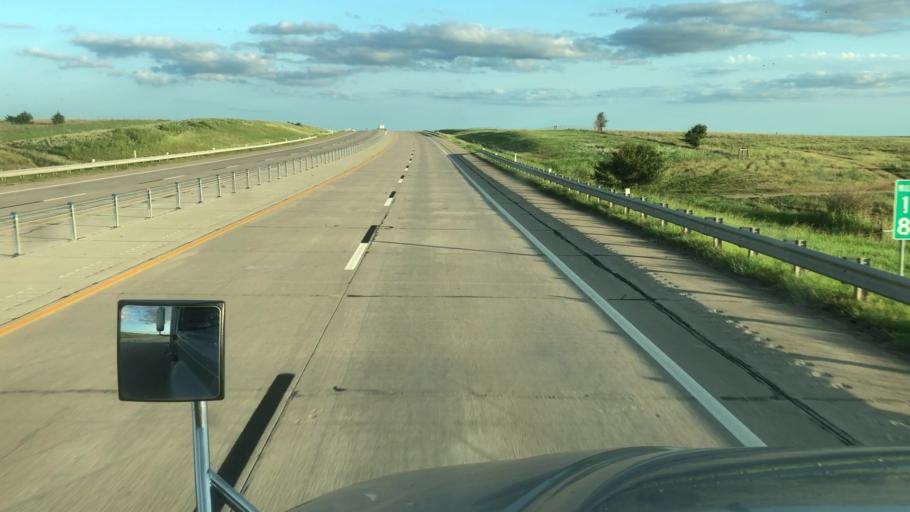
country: US
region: Oklahoma
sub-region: Pawnee County
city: Pawnee
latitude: 36.3515
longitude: -97.0298
